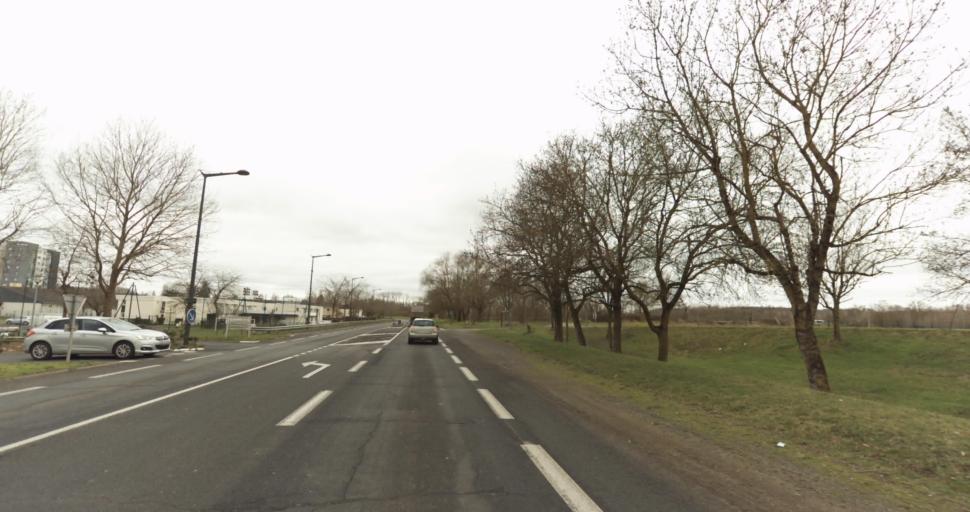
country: FR
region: Pays de la Loire
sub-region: Departement de Maine-et-Loire
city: Saumur
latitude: 47.2427
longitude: -0.0795
